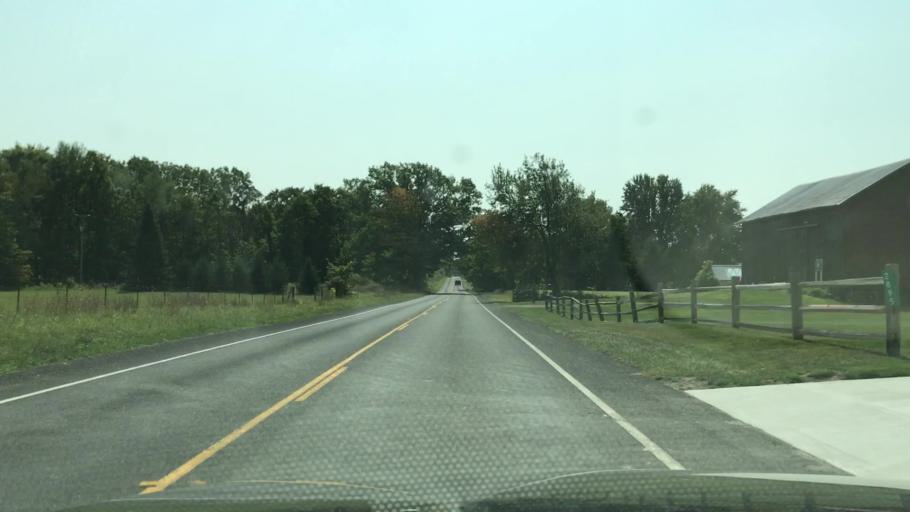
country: US
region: Michigan
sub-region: Kent County
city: Byron Center
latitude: 42.8205
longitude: -85.7829
